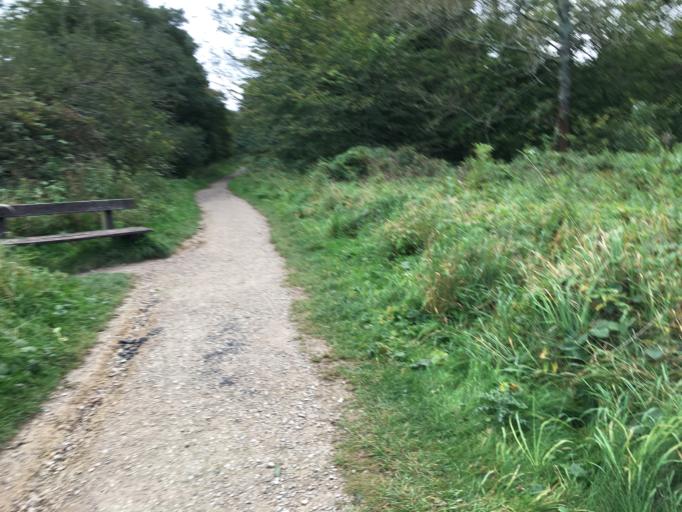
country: GB
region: England
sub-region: North Yorkshire
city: Sleights
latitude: 54.4070
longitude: -0.7344
